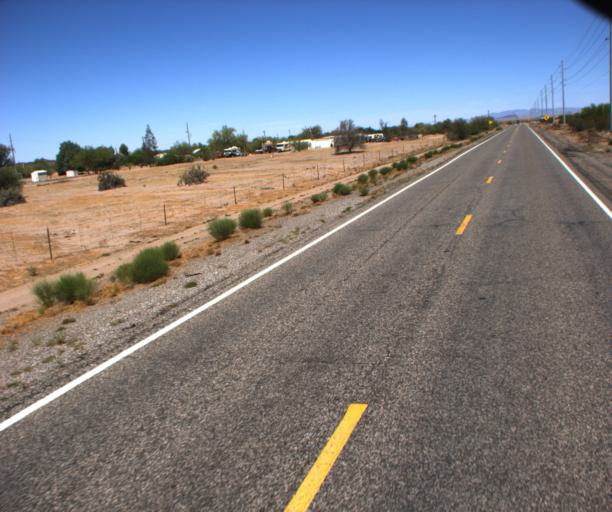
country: US
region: Arizona
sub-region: La Paz County
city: Cienega Springs
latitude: 33.9545
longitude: -114.0251
